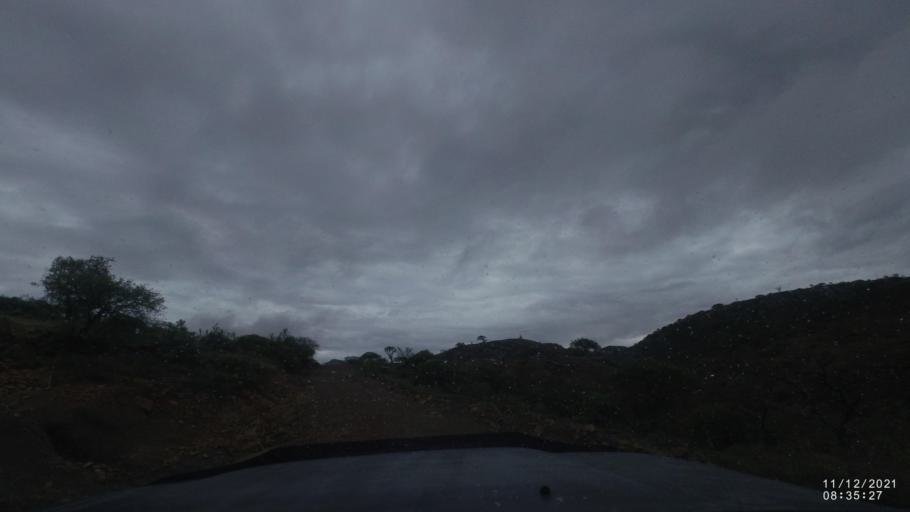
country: BO
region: Cochabamba
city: Tarata
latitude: -17.9304
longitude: -65.9358
